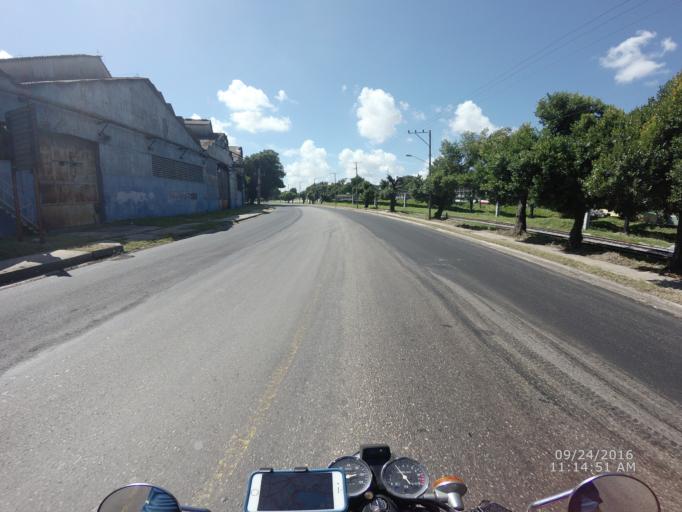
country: CU
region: La Habana
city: La Habana Vieja
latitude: 23.1219
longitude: -82.3598
